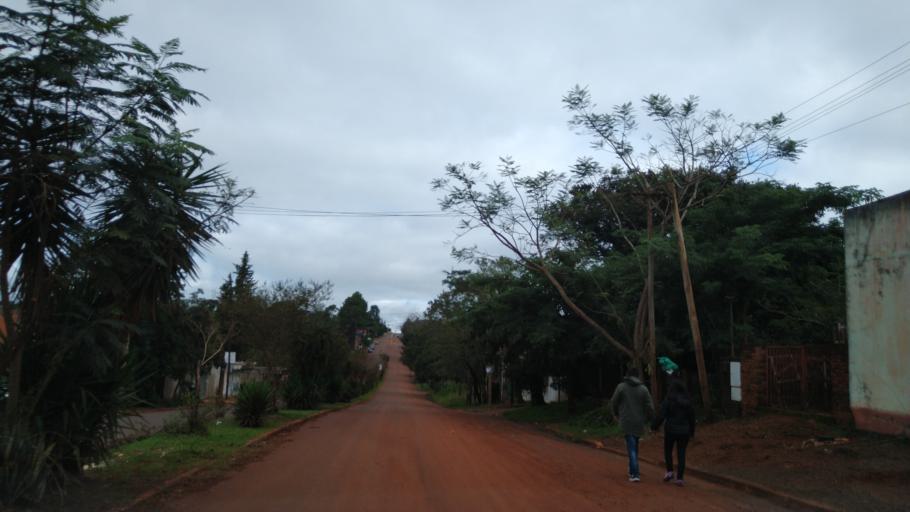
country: AR
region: Misiones
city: Jardin America
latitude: -27.0368
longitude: -55.2351
